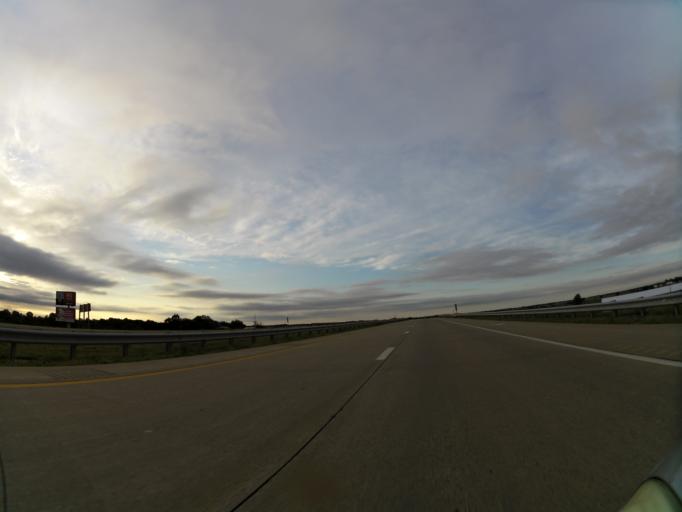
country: US
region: Kansas
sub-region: Reno County
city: South Hutchinson
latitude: 37.9419
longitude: -97.8824
